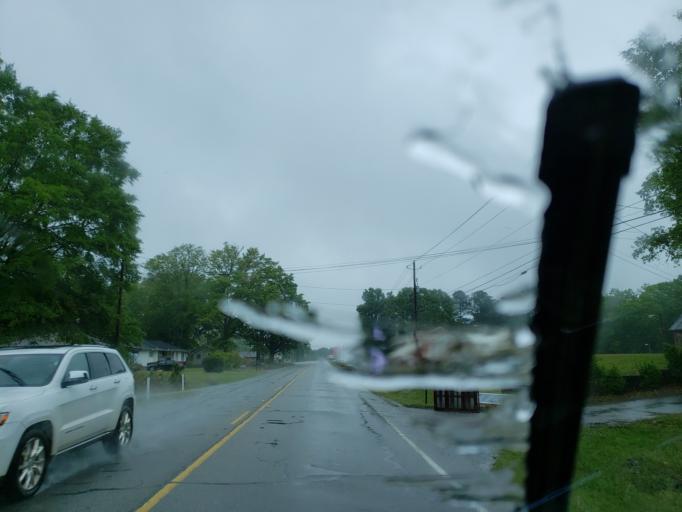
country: US
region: Georgia
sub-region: Carroll County
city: Villa Rica
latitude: 33.7411
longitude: -84.9206
